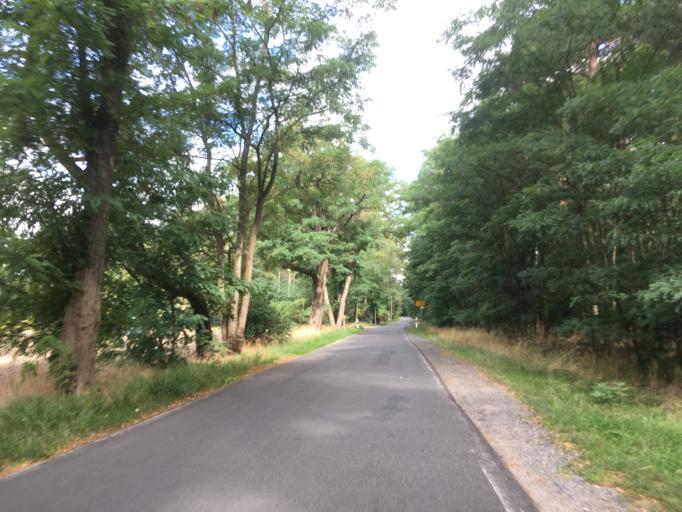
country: DE
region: Brandenburg
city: Bestensee
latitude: 52.2639
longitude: 13.7619
